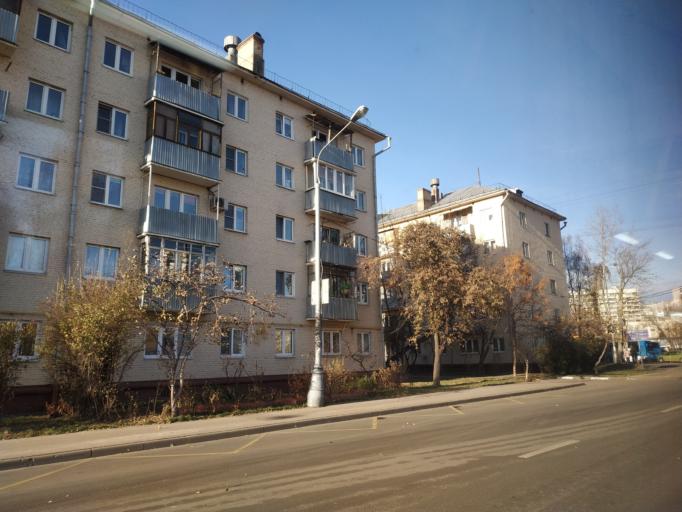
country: RU
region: Moscow
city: Biryulevo
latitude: 55.5801
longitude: 37.6769
